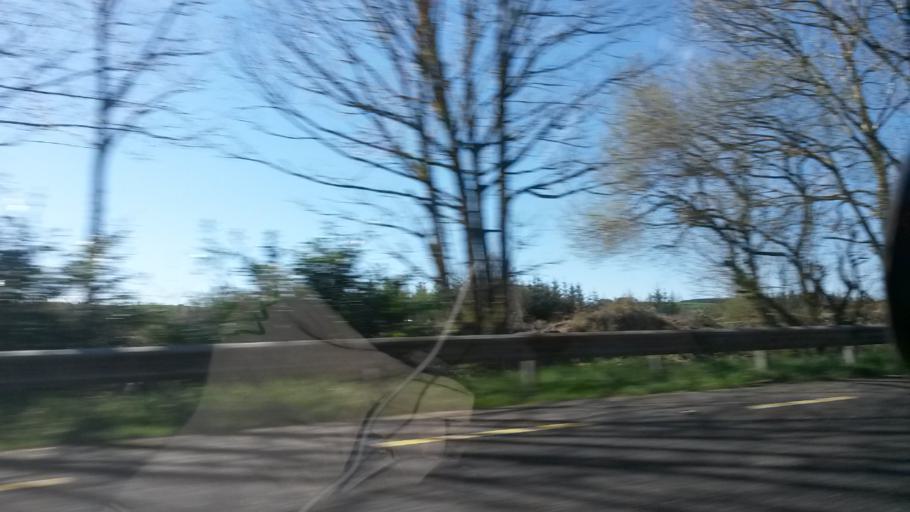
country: IE
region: Munster
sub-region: County Cork
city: Macroom
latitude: 51.9110
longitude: -9.0291
